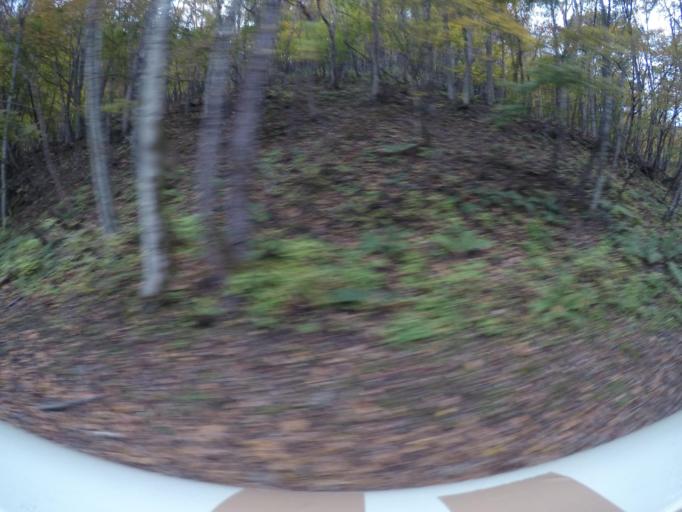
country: JP
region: Nagano
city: Saku
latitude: 36.0720
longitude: 138.6468
